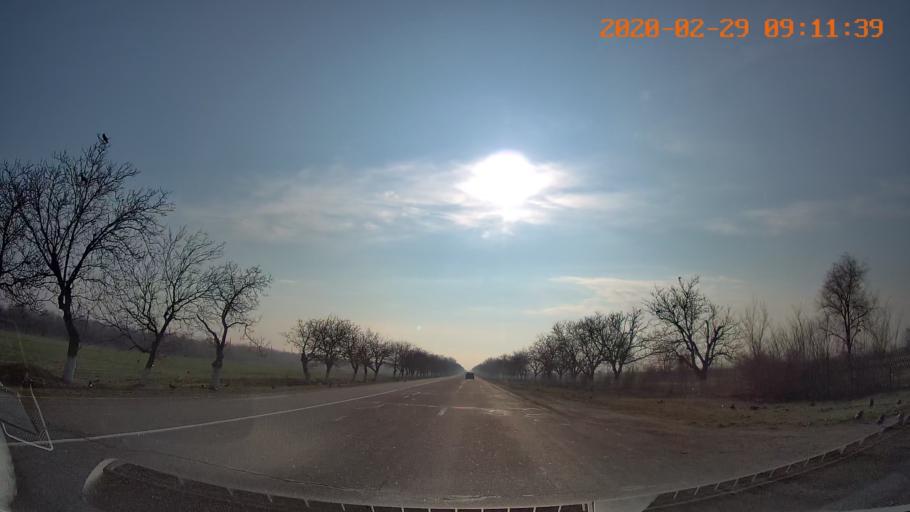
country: MD
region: Telenesti
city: Slobozia
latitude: 46.8332
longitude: 29.8037
